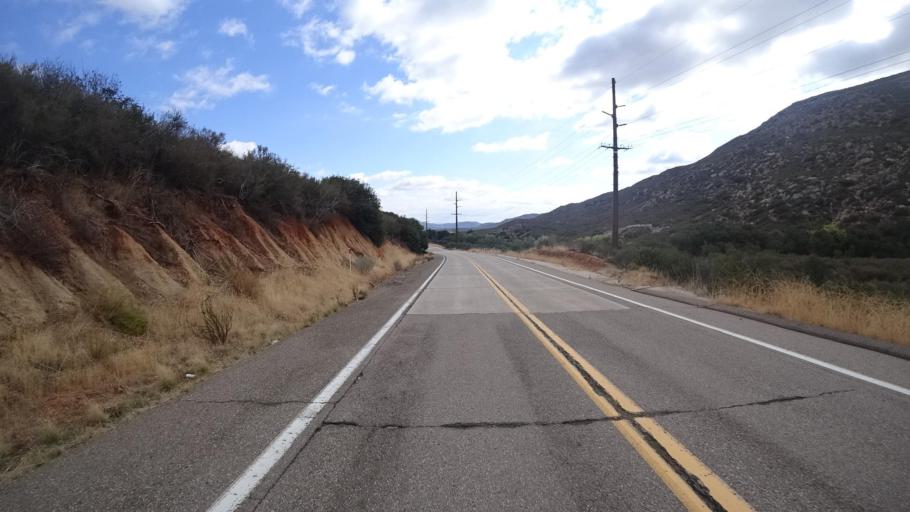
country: US
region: California
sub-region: San Diego County
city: Pine Valley
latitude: 32.7769
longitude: -116.4939
